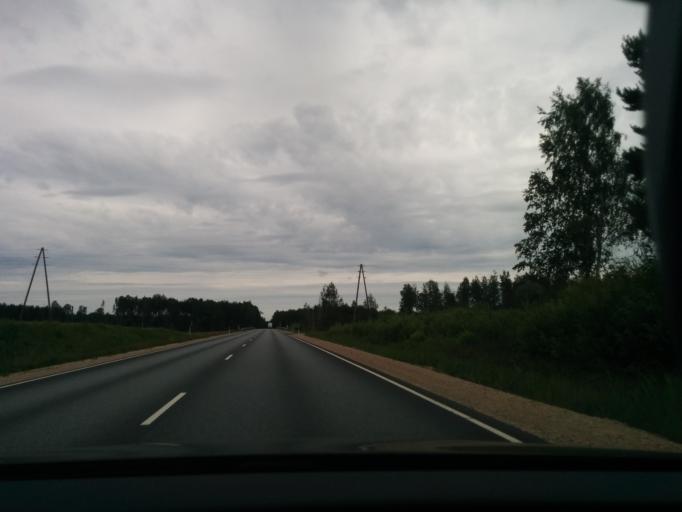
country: LV
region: Ikskile
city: Ikskile
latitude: 56.8834
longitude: 24.5020
